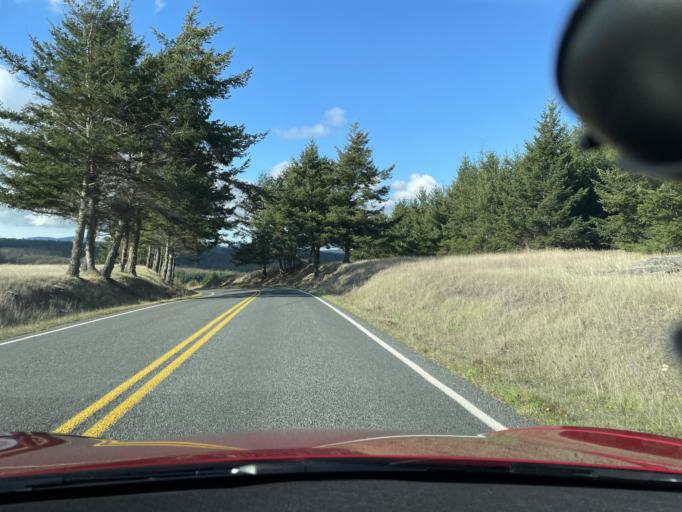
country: US
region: Washington
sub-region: San Juan County
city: Friday Harbor
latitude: 48.4626
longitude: -122.9980
